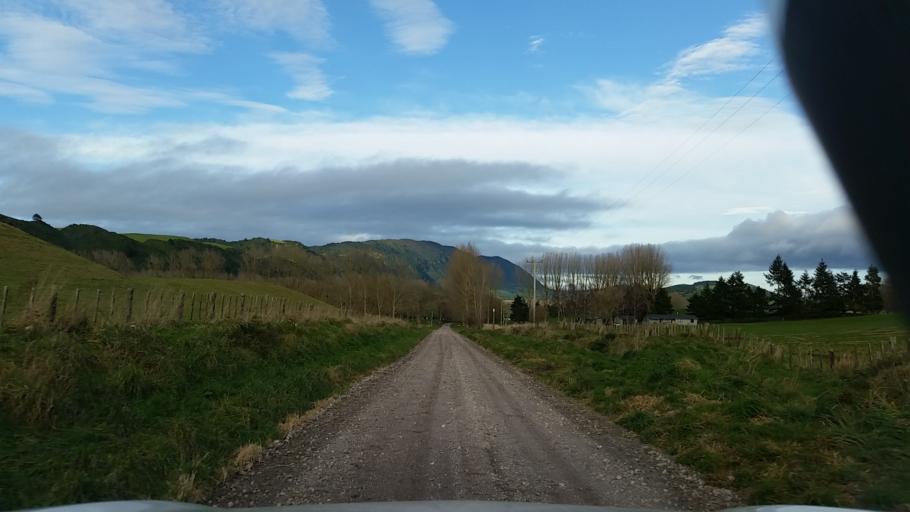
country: NZ
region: Bay of Plenty
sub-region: Rotorua District
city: Rotorua
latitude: -38.3193
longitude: 176.2988
